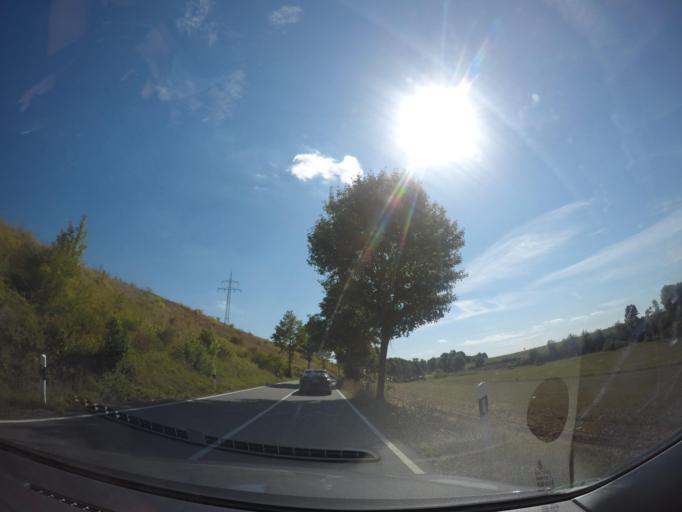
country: DE
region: Lower Saxony
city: Bad Lauterberg im Harz
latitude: 51.6053
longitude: 10.4730
